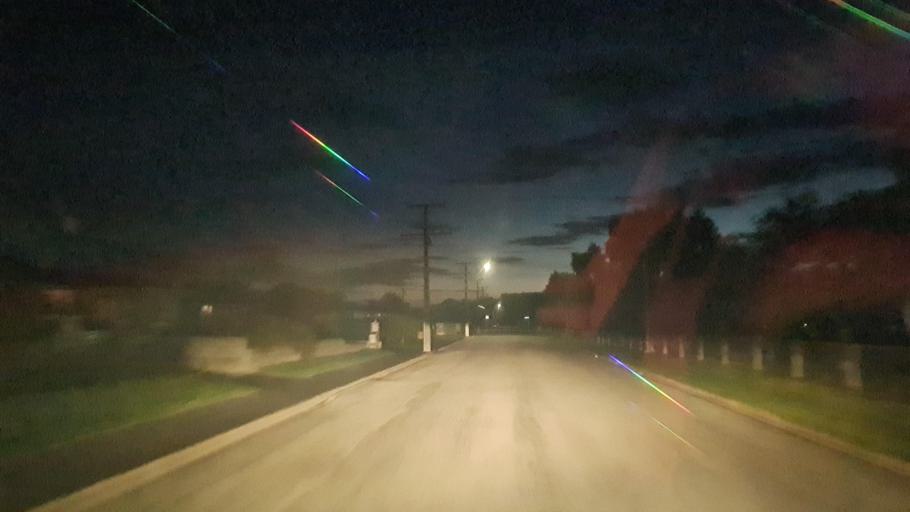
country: NZ
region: Otago
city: Oamaru
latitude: -45.0672
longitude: 170.9879
